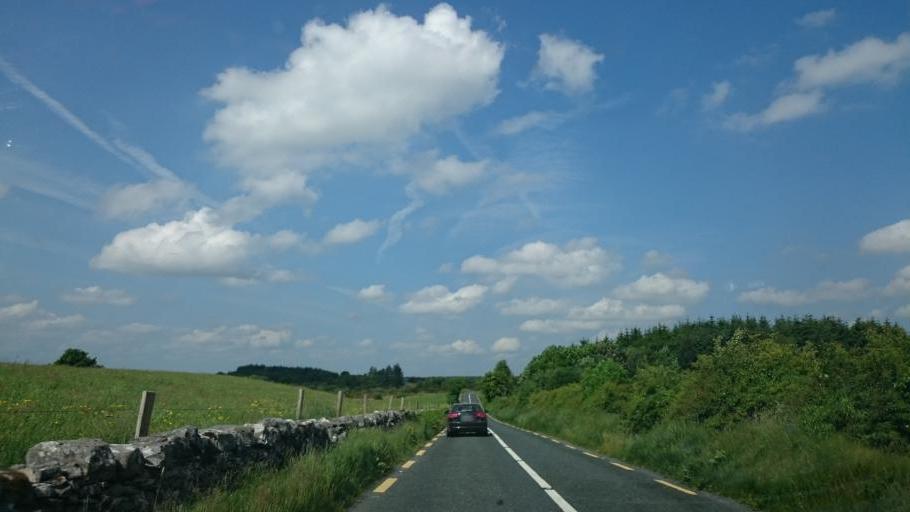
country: IE
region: Connaught
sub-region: Maigh Eo
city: Ballyhaunis
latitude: 53.8785
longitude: -8.7800
